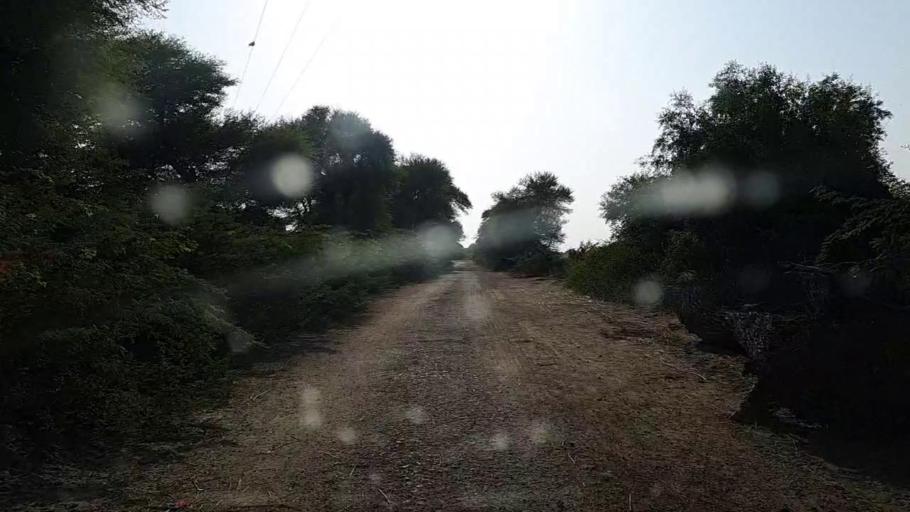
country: PK
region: Sindh
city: Bulri
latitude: 24.7689
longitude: 68.4331
